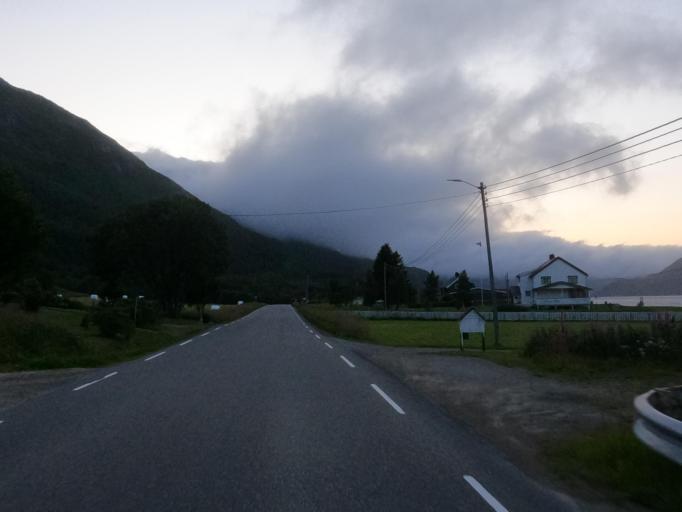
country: NO
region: Nordland
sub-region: Lodingen
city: Lodingen
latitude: 68.5684
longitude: 15.7986
